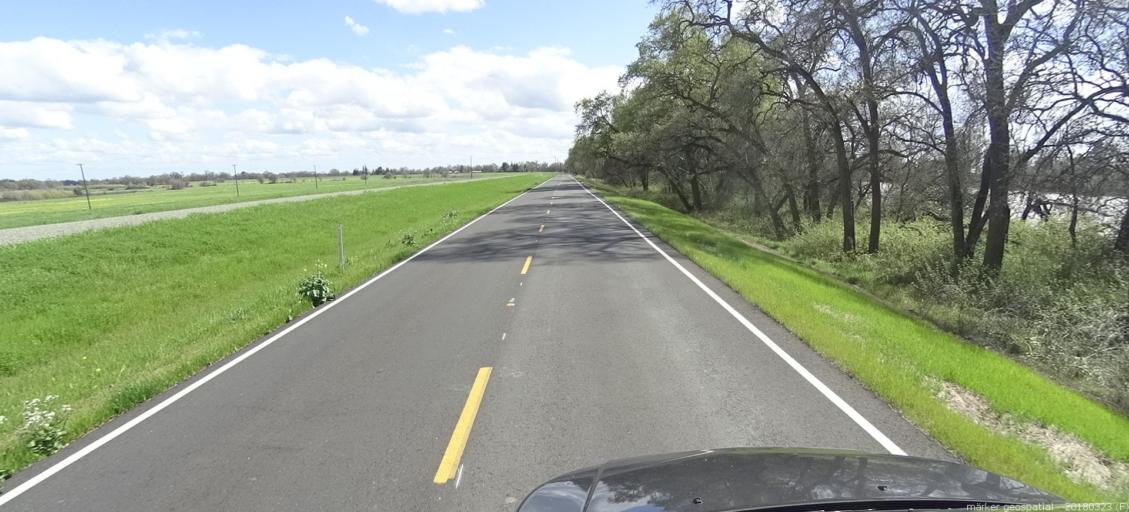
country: US
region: California
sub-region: Yolo County
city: West Sacramento
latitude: 38.6529
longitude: -121.6000
